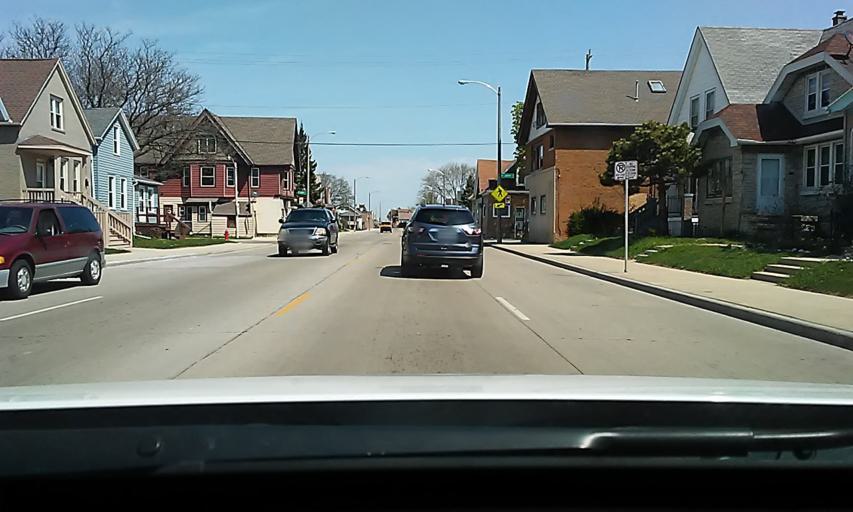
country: US
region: Wisconsin
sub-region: Milwaukee County
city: West Milwaukee
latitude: 43.0135
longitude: -87.9575
